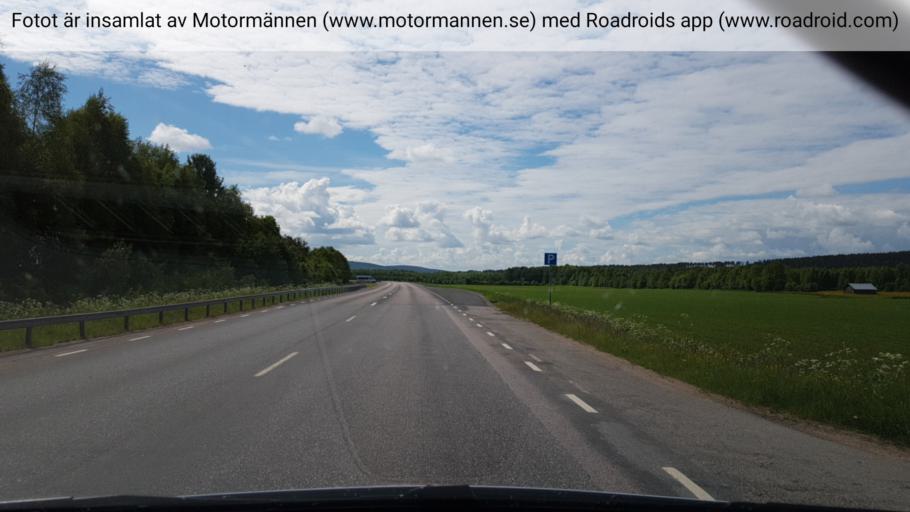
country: SE
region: Norrbotten
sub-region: Overtornea Kommun
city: OEvertornea
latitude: 66.4196
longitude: 23.6276
